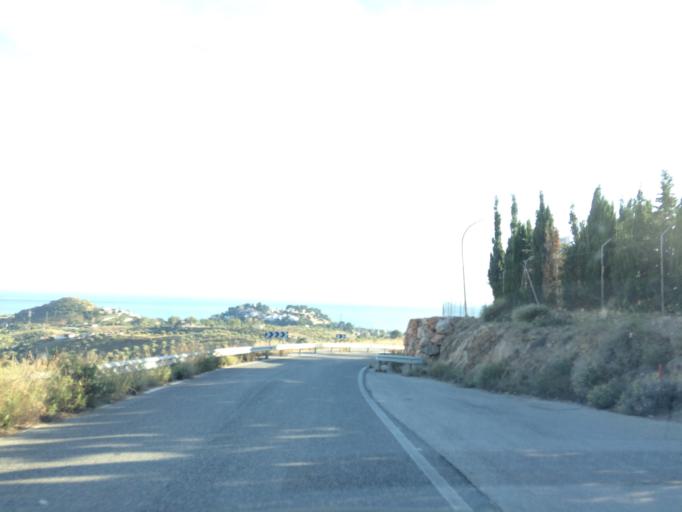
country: ES
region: Andalusia
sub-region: Provincia de Malaga
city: Totalan
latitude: 36.7335
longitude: -4.3369
